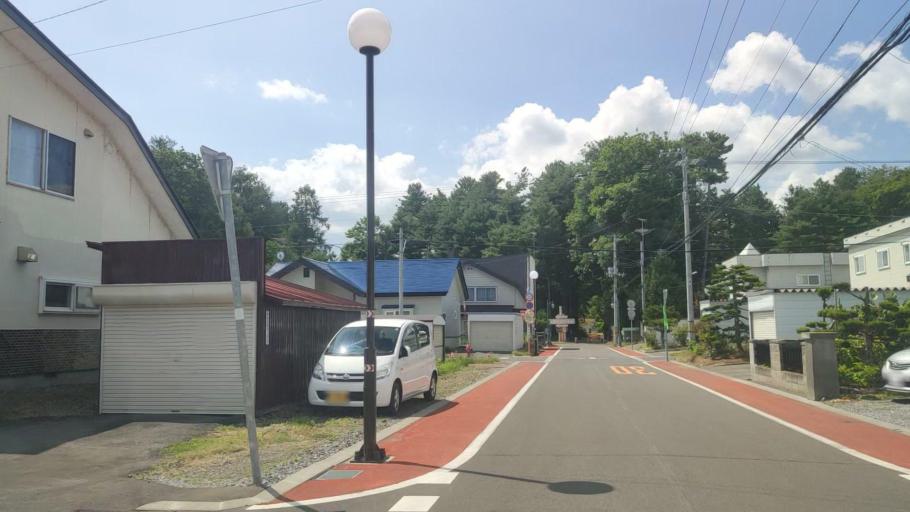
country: JP
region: Hokkaido
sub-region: Asahikawa-shi
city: Asahikawa
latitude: 43.7541
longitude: 142.3492
